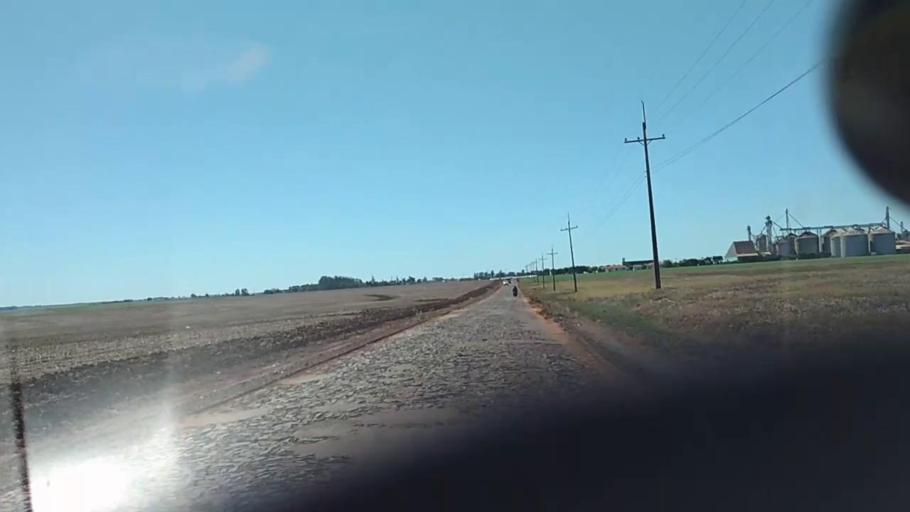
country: PY
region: Alto Parana
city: Naranjal
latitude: -25.9742
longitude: -55.1558
